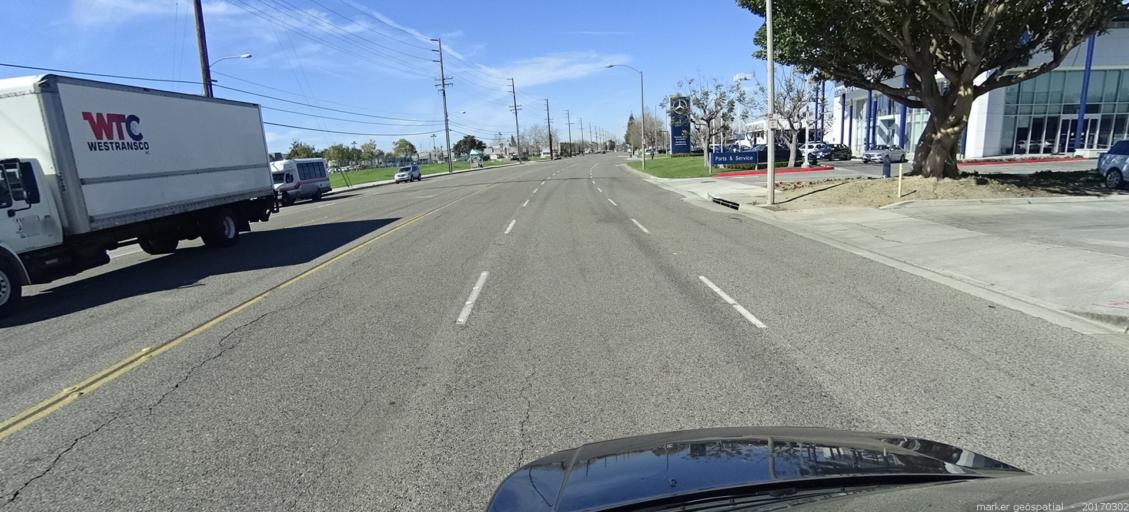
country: US
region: California
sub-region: Orange County
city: Yorba Linda
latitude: 33.8597
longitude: -117.7979
